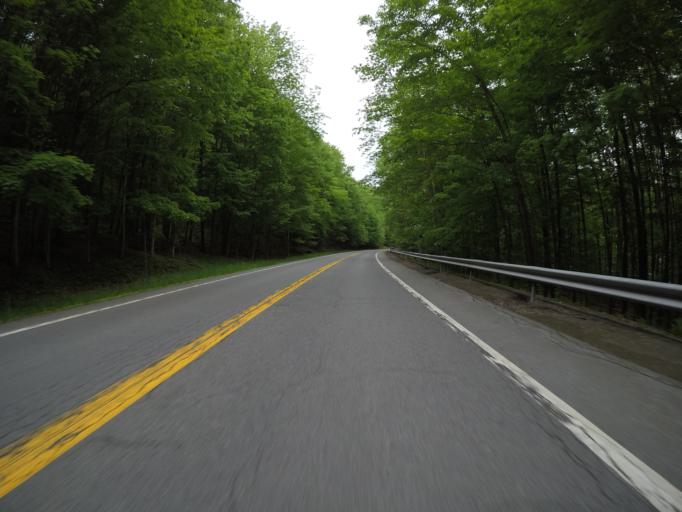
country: US
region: New York
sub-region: Sullivan County
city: Livingston Manor
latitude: 42.0797
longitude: -74.8789
